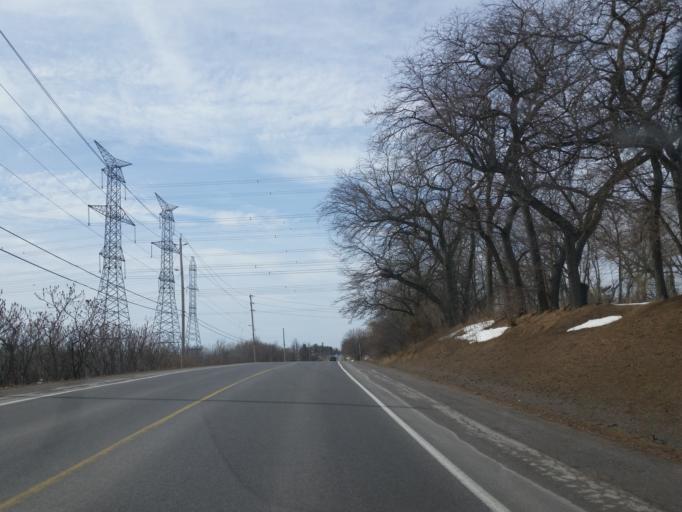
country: CA
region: Ontario
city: Napanee Downtown
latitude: 44.2126
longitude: -76.9894
